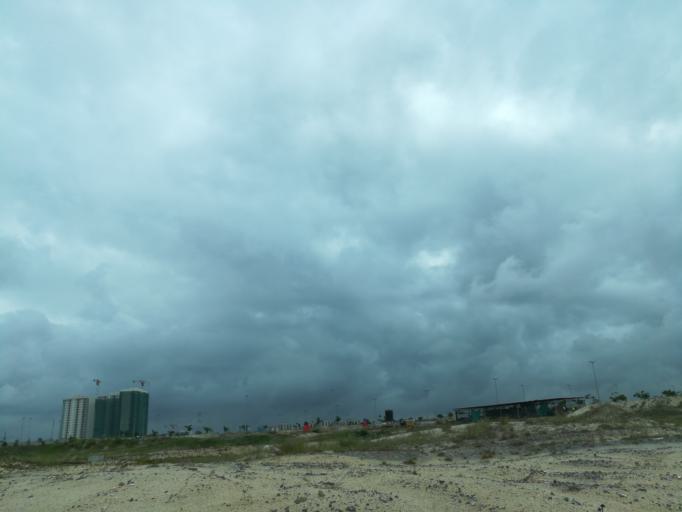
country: NG
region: Lagos
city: Lagos
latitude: 6.4126
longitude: 3.4130
